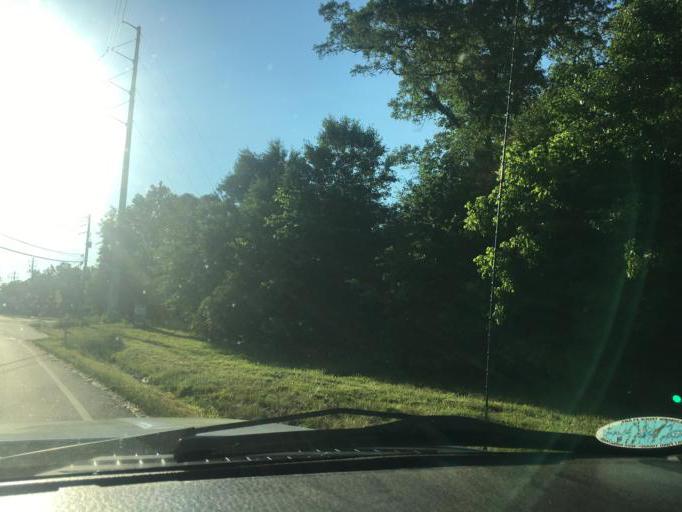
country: US
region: Georgia
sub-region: Forsyth County
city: Cumming
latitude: 34.2725
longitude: -84.1036
